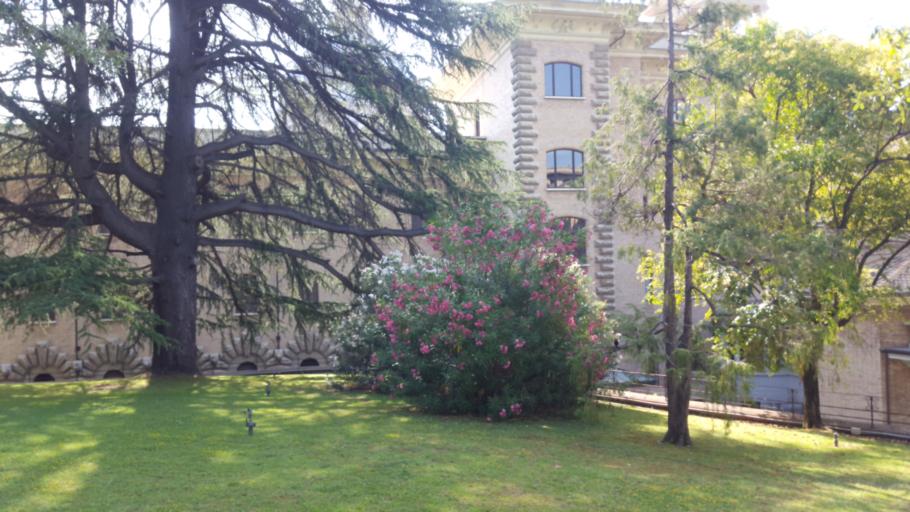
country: VA
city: Vatican City
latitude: 41.9028
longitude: 12.4507
